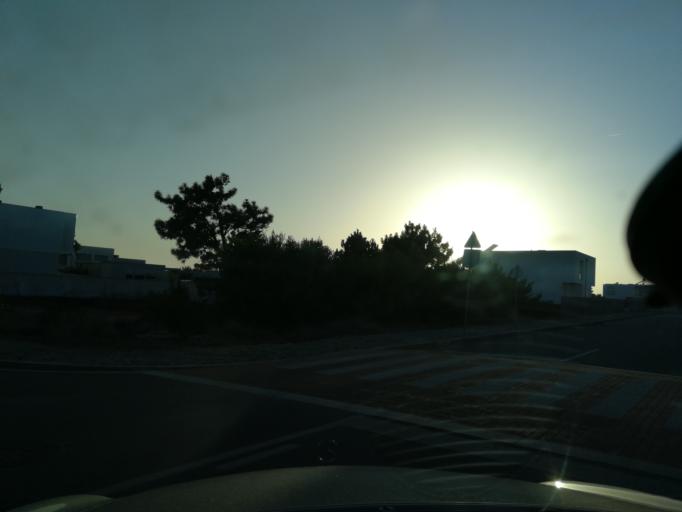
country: PT
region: Aveiro
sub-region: Murtosa
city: Murtosa
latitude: 40.7567
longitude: -8.7055
